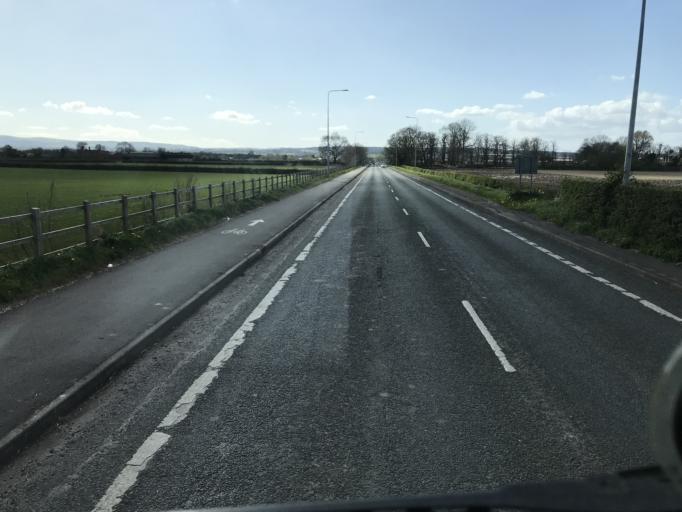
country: GB
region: England
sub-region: Cheshire West and Chester
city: Blacon
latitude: 53.1749
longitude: -2.9500
